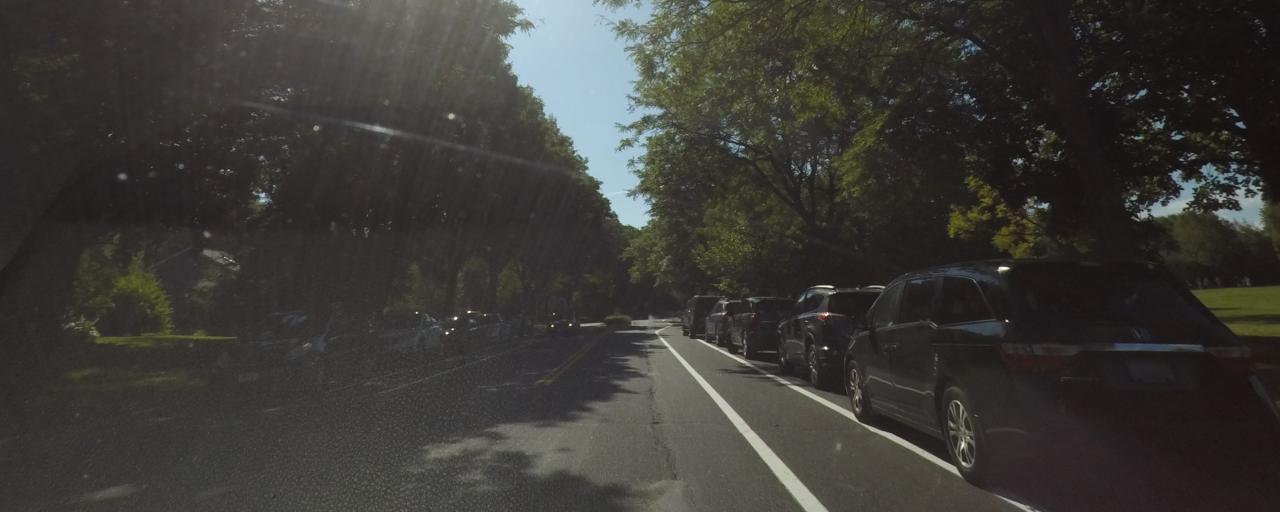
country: US
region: Wisconsin
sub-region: Dane County
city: Middleton
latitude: 43.0695
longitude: -89.5095
